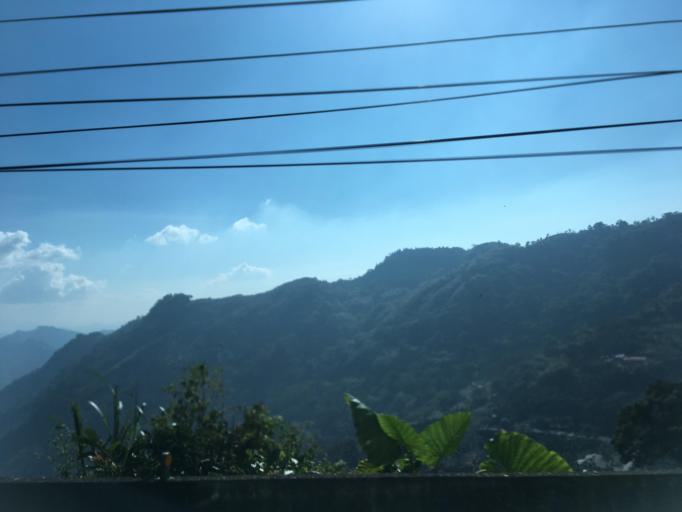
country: TW
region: Taiwan
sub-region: Chiayi
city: Jiayi Shi
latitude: 23.4051
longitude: 120.6543
